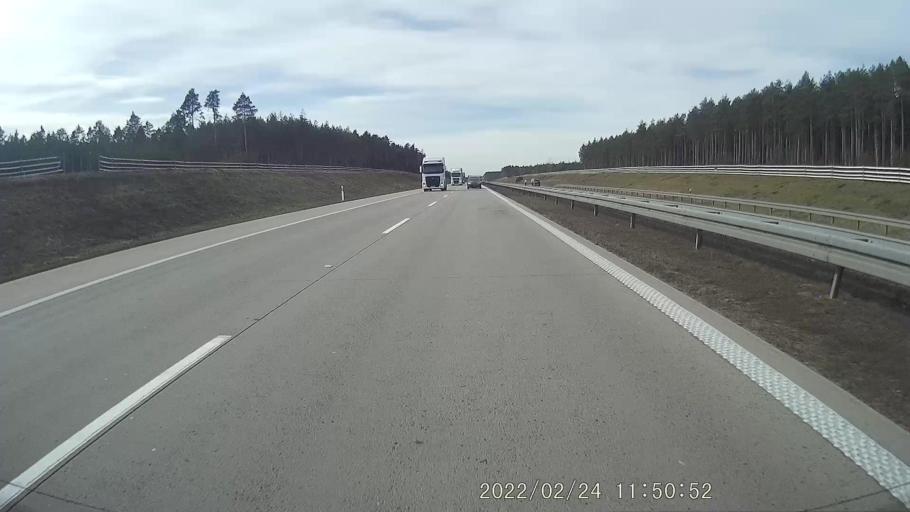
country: PL
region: Lower Silesian Voivodeship
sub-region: Powiat polkowicki
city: Radwanice
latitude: 51.6056
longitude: 15.9659
